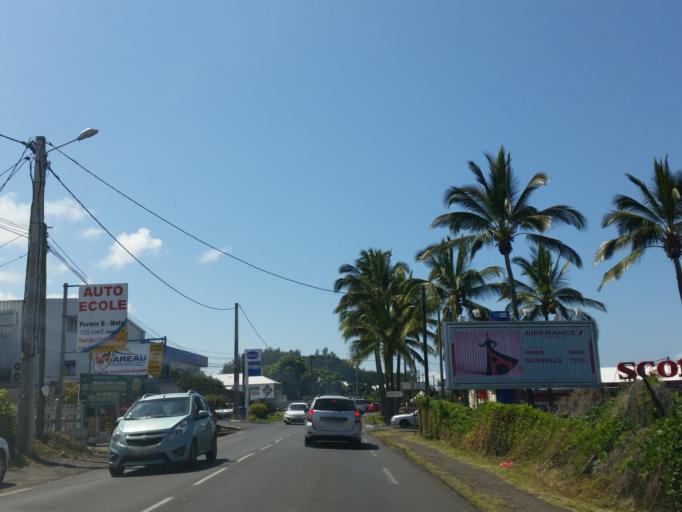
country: RE
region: Reunion
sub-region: Reunion
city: Saint-Joseph
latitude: -21.3804
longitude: 55.6087
